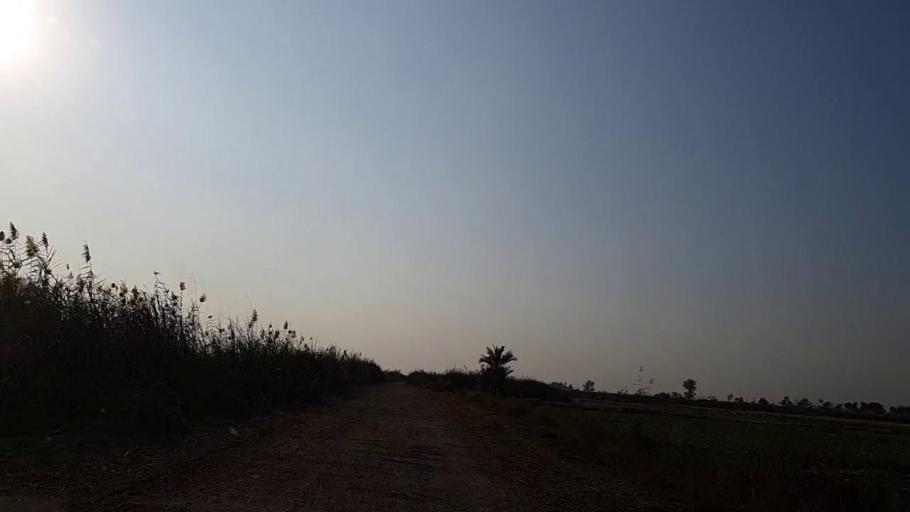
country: PK
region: Sindh
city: Sakrand
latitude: 26.0906
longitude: 68.3905
